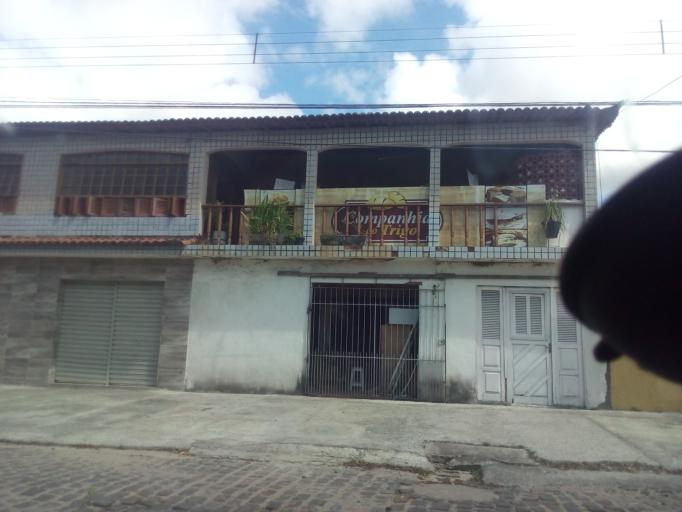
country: BR
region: Rio Grande do Norte
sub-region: Natal
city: Natal
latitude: -5.8250
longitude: -35.2390
